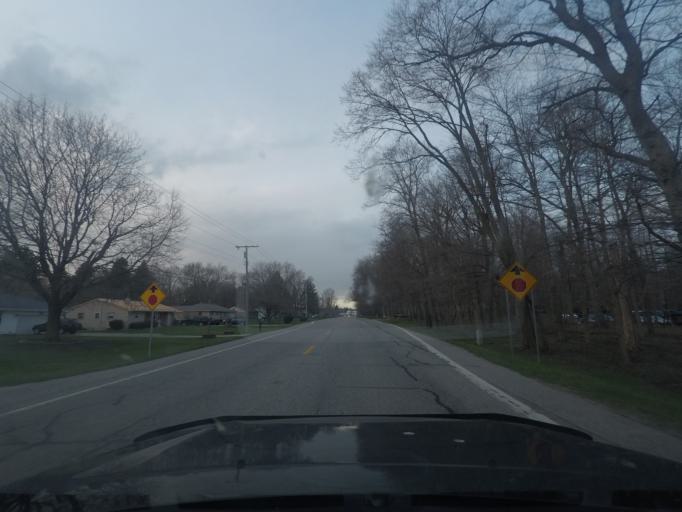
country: US
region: Indiana
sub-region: LaPorte County
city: LaPorte
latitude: 41.5951
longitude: -86.7392
